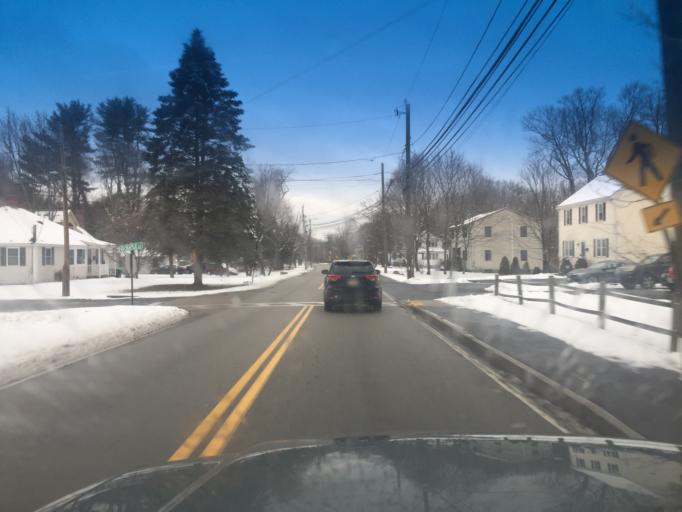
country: US
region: Massachusetts
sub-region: Norfolk County
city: Millis
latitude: 42.1776
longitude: -71.3608
